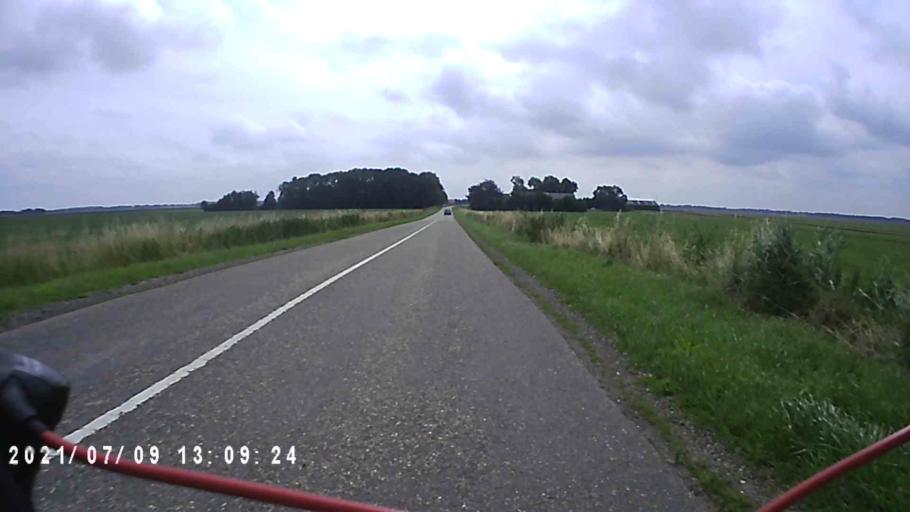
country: NL
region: Groningen
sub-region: Gemeente  Oldambt
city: Winschoten
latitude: 53.1296
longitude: 7.1174
